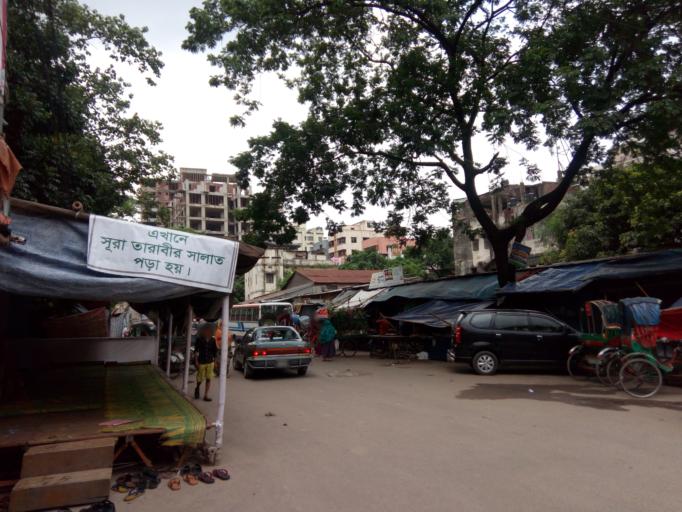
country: BD
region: Dhaka
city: Paltan
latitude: 23.7216
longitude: 90.4241
